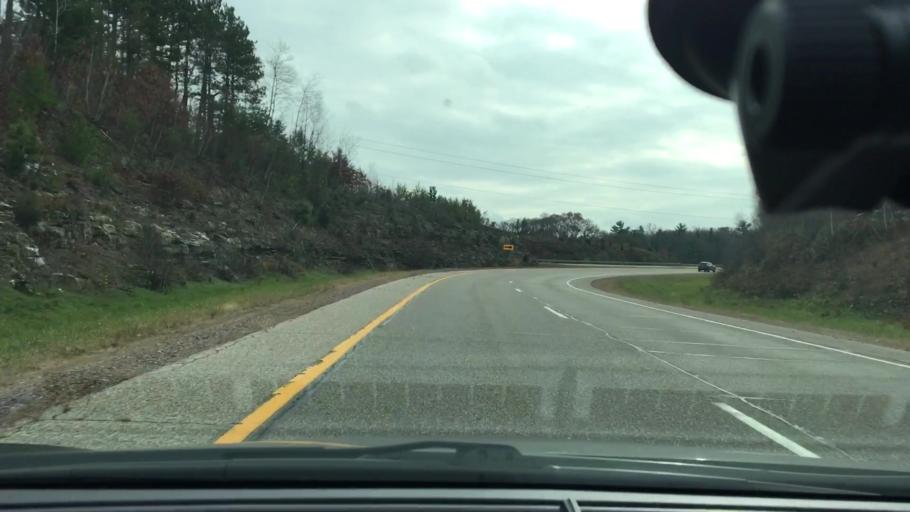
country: US
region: Wisconsin
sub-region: Sauk County
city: Lake Delton
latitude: 43.6221
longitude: -89.8057
